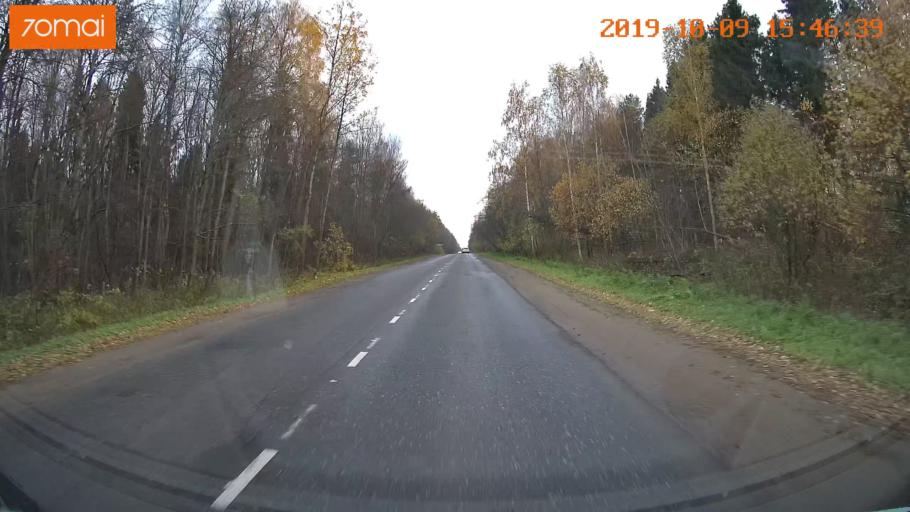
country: RU
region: Kostroma
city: Oktyabr'skiy
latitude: 57.8231
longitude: 41.0405
